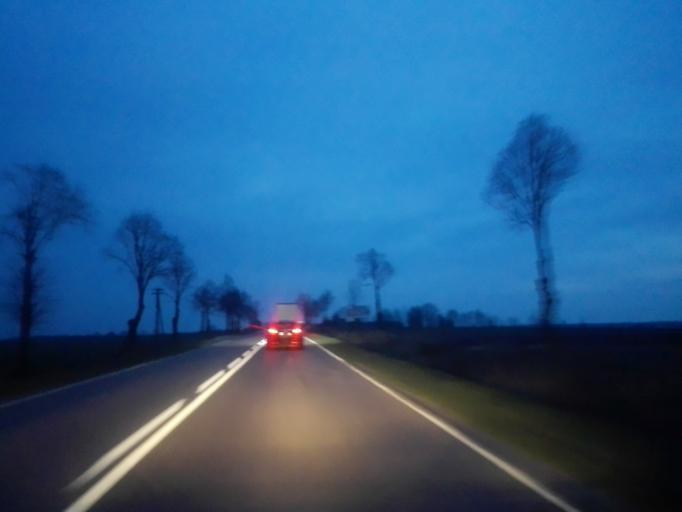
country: PL
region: Podlasie
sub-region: Lomza
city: Lomza
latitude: 53.1200
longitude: 22.0324
